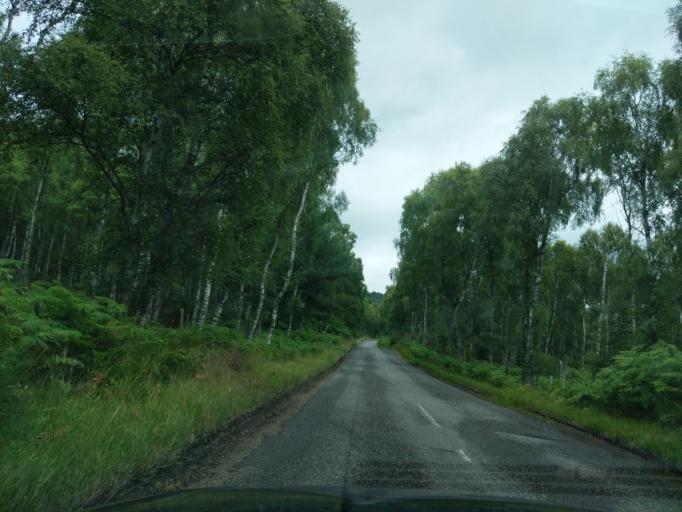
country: GB
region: Scotland
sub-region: Aberdeenshire
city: Ballater
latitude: 57.0685
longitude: -2.9476
